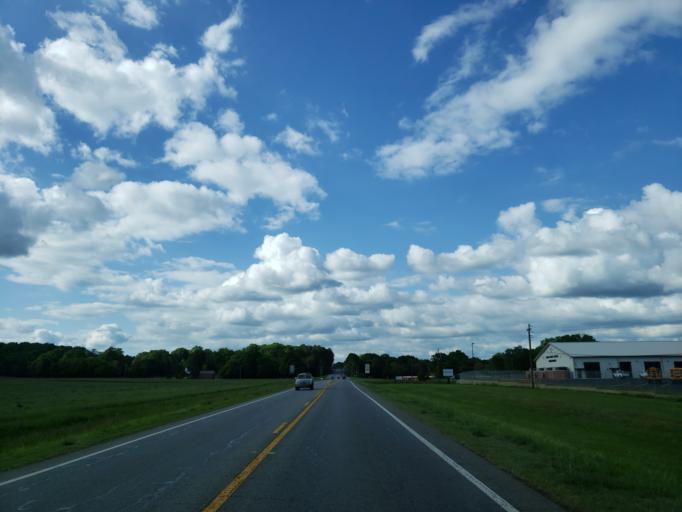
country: US
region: Georgia
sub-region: Bartow County
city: Cartersville
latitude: 34.2407
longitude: -84.8568
